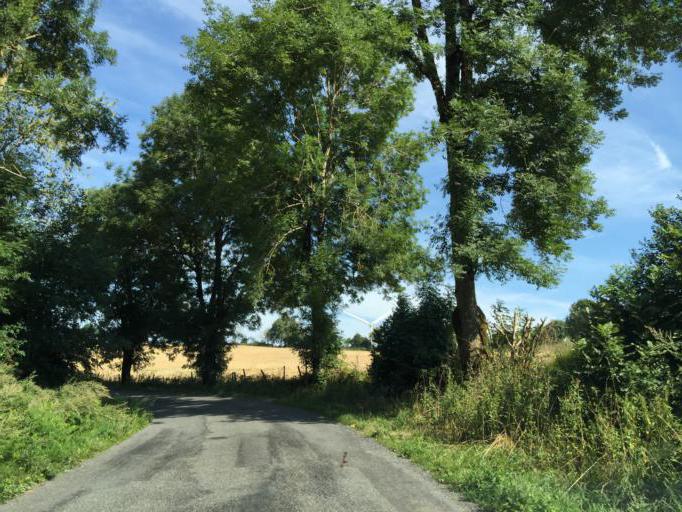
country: FR
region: Midi-Pyrenees
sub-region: Departement de l'Aveyron
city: Pont-de-Salars
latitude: 44.3114
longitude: 2.7045
